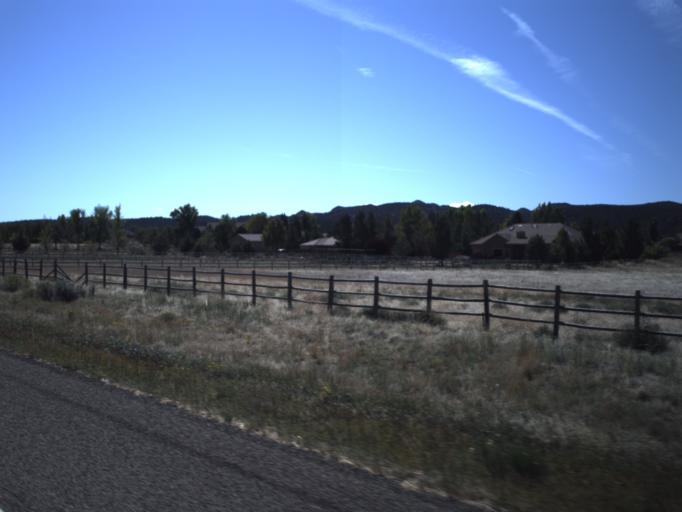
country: US
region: Utah
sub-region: Washington County
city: Ivins
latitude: 37.3030
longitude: -113.6689
